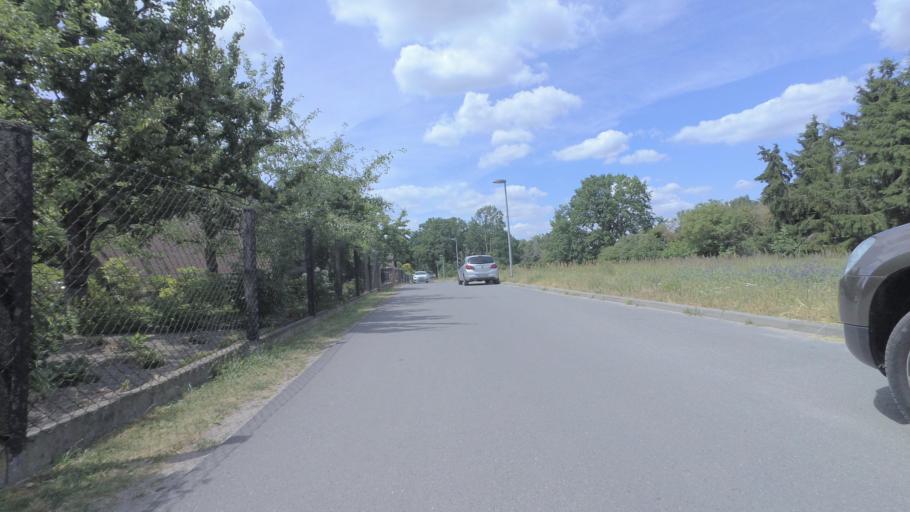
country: DE
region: Brandenburg
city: Teltow
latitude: 52.3687
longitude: 13.2586
